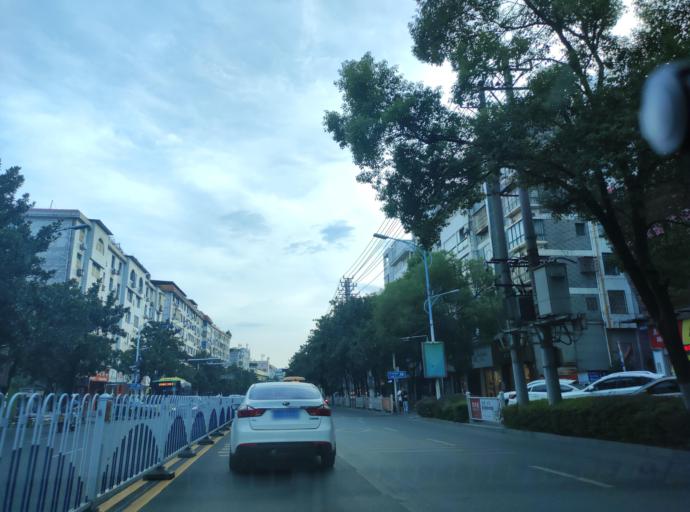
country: CN
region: Jiangxi Sheng
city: Pingxiang
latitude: 27.6337
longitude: 113.8555
